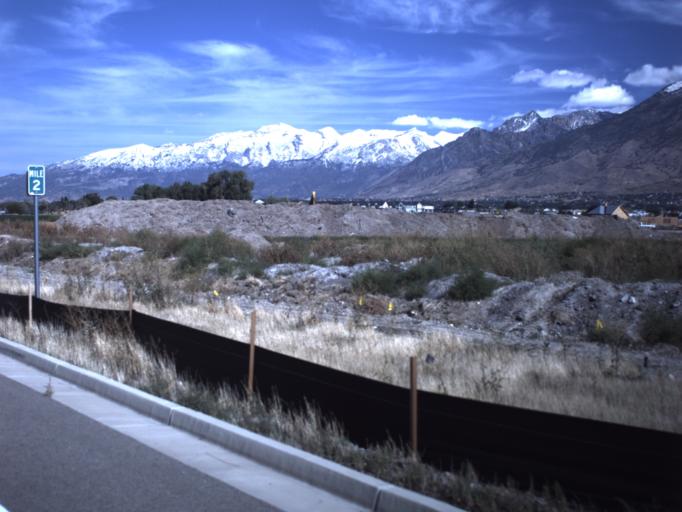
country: US
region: Utah
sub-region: Utah County
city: Pleasant Grove
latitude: 40.3562
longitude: -111.7671
